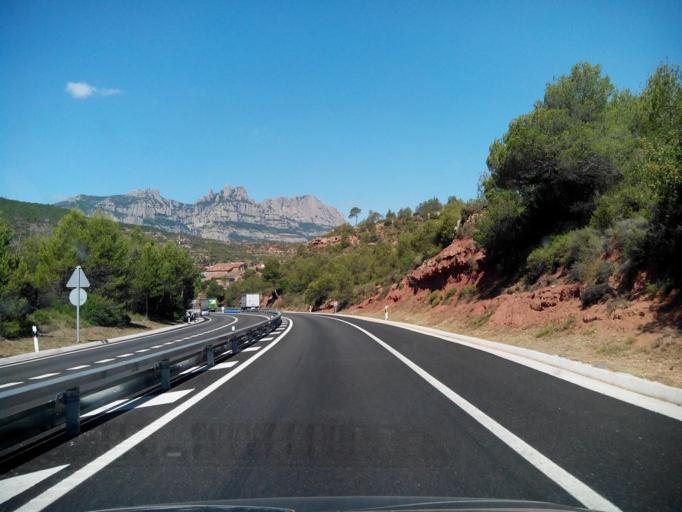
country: ES
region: Catalonia
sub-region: Provincia de Barcelona
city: Olesa de Montserrat
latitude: 41.5908
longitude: 1.9053
